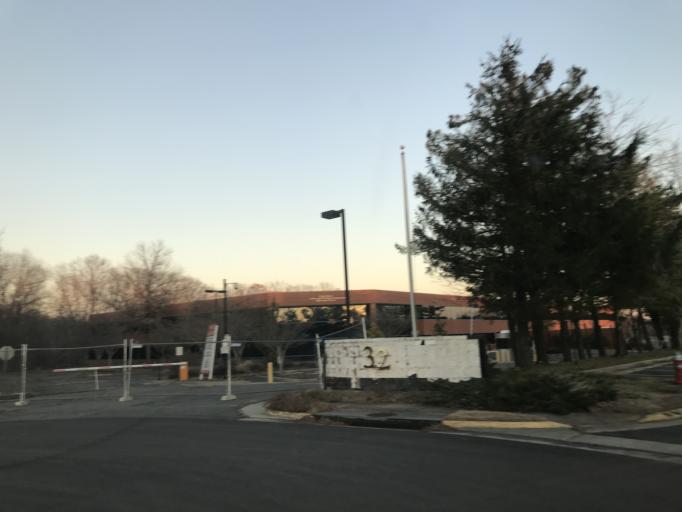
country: US
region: Virginia
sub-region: Fairfax County
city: Franconia
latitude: 38.7959
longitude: -77.1619
